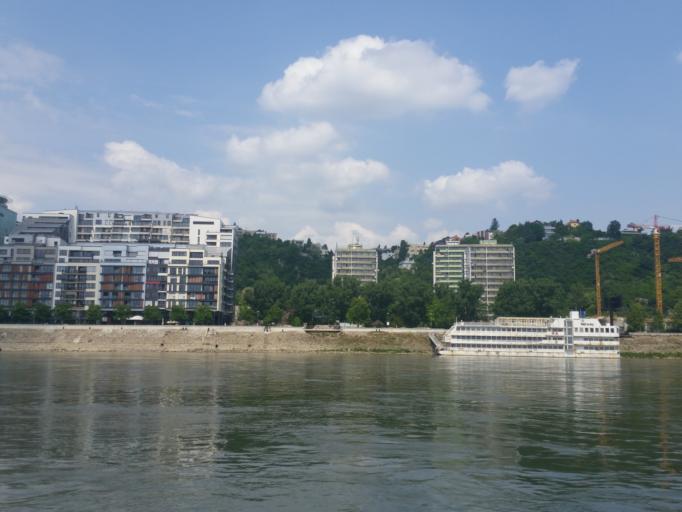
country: SK
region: Bratislavsky
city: Bratislava
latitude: 48.1386
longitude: 17.0910
